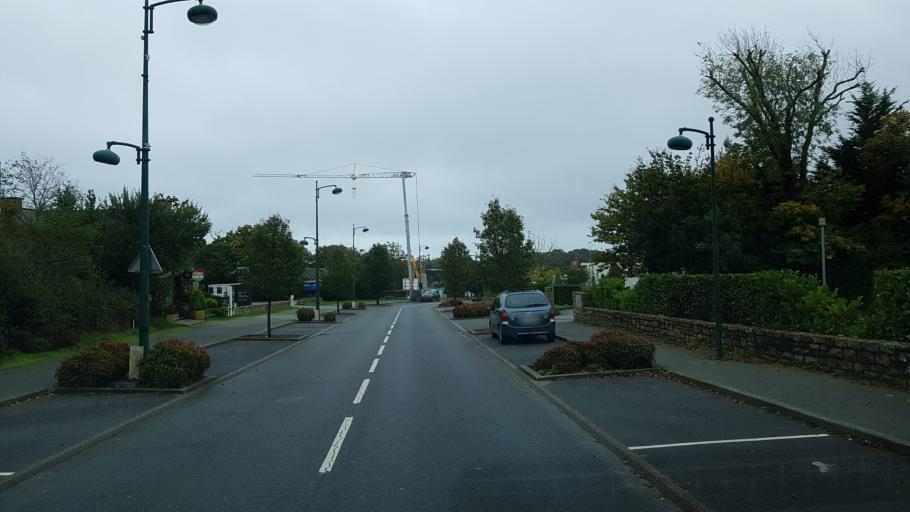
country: FR
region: Brittany
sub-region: Departement du Morbihan
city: Sarzeau
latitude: 47.5239
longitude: -2.7686
